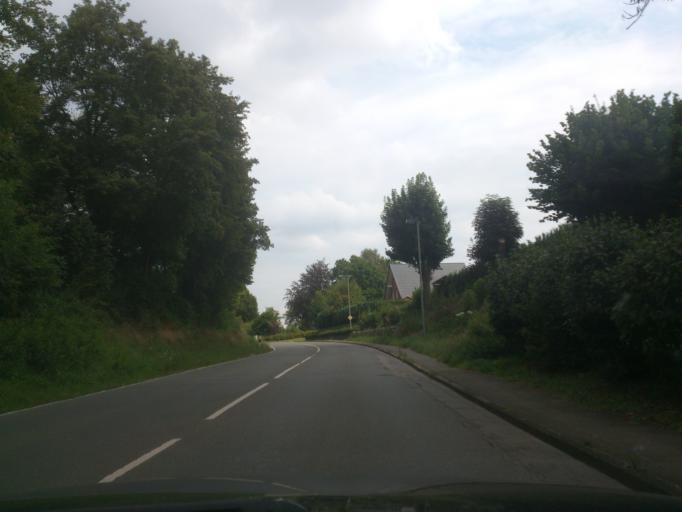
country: DE
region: North Rhine-Westphalia
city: Brakel
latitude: 51.7010
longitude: 9.1620
